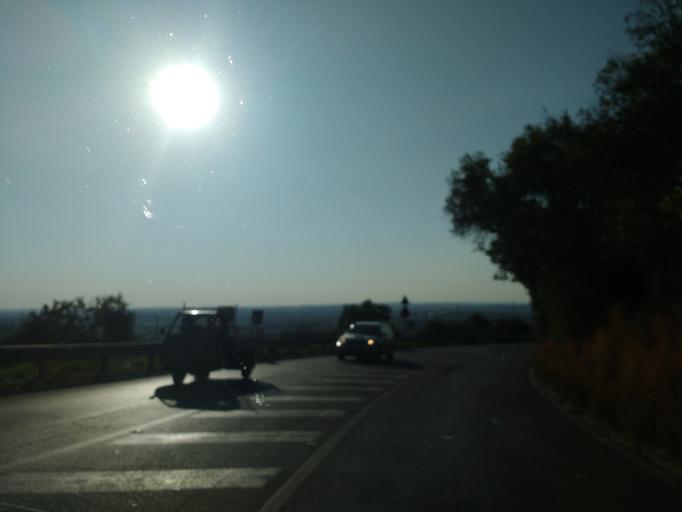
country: IT
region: Latium
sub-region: Citta metropolitana di Roma Capitale
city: Tivoli
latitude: 41.9486
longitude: 12.7906
